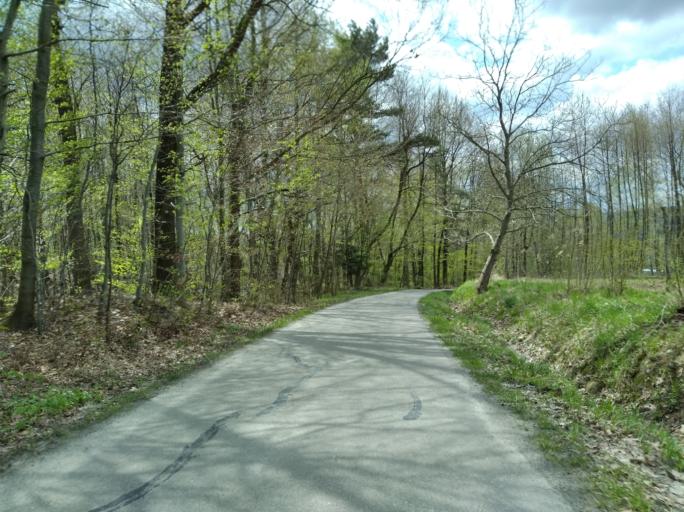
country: PL
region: Subcarpathian Voivodeship
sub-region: Powiat strzyzowski
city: Niebylec
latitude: 49.8851
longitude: 21.9259
